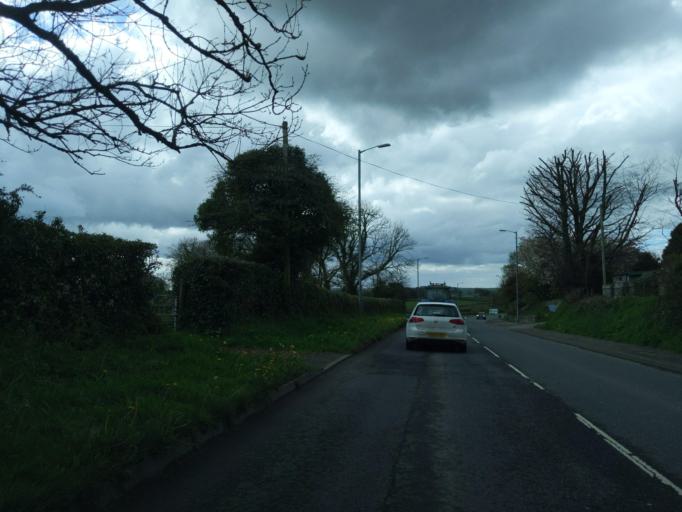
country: GB
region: England
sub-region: Cornwall
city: Callington
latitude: 50.4982
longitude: -4.3132
